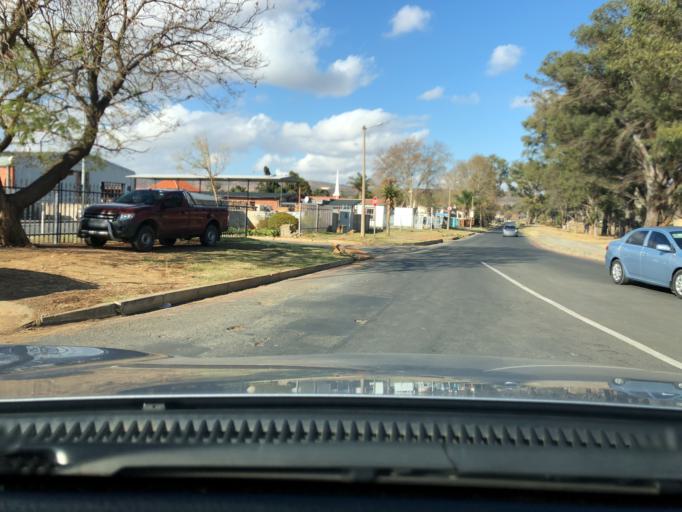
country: ZA
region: KwaZulu-Natal
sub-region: uThukela District Municipality
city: Ladysmith
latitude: -28.5613
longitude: 29.7780
